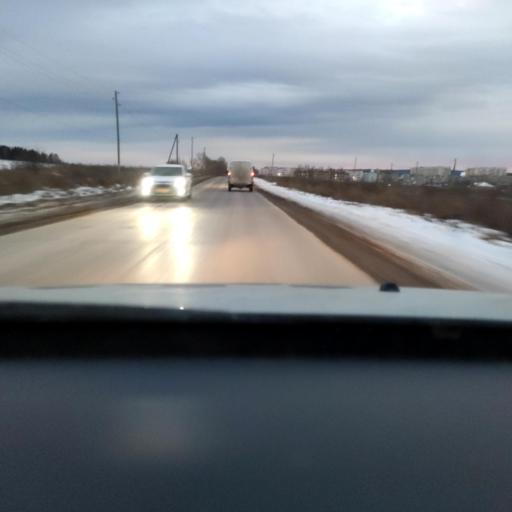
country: RU
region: Perm
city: Gamovo
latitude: 57.8793
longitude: 56.1017
